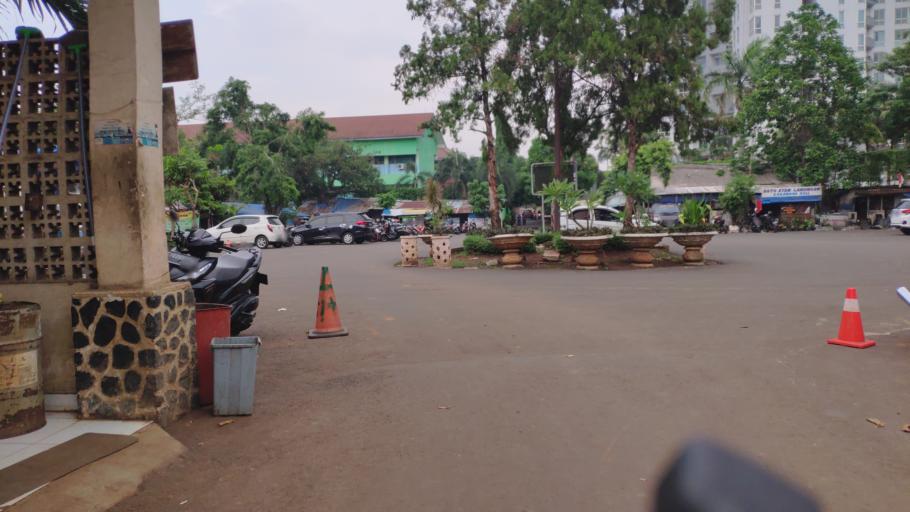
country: ID
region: Jakarta Raya
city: Jakarta
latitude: -6.2230
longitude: 106.8373
